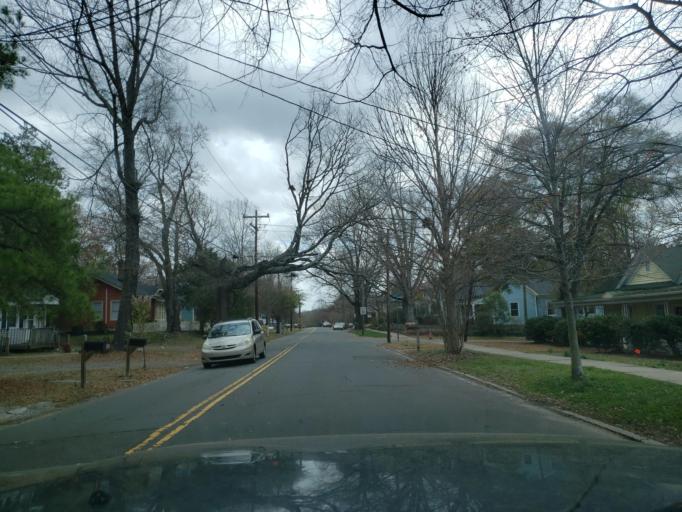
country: US
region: North Carolina
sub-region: Durham County
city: Durham
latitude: 35.9868
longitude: -78.9259
